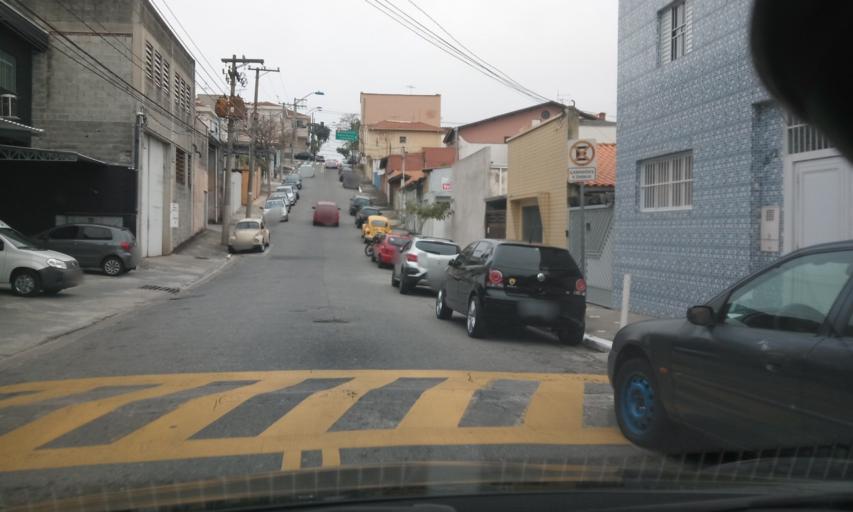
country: BR
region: Sao Paulo
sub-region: Sao Caetano Do Sul
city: Sao Caetano do Sul
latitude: -23.6258
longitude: -46.5734
